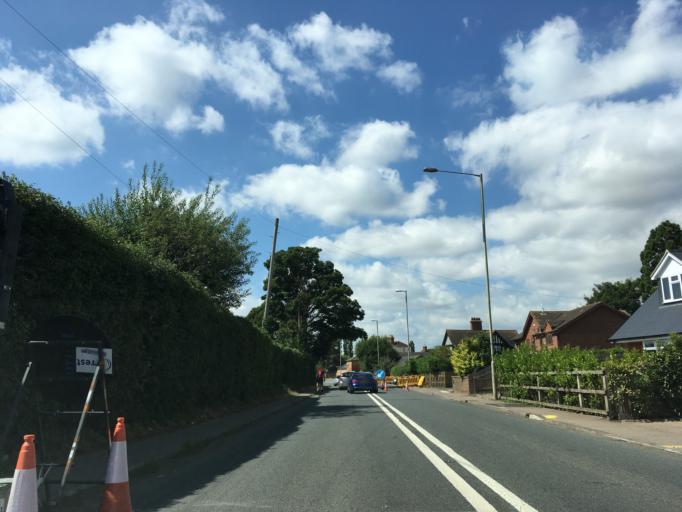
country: GB
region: England
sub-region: Gloucestershire
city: Gloucester
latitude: 51.8988
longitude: -2.2234
